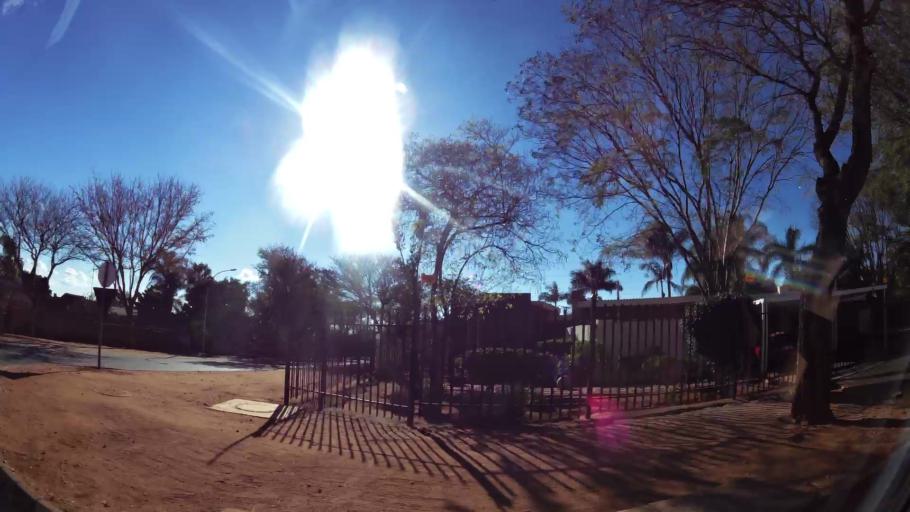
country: ZA
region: Limpopo
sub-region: Capricorn District Municipality
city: Polokwane
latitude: -23.8944
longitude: 29.4829
